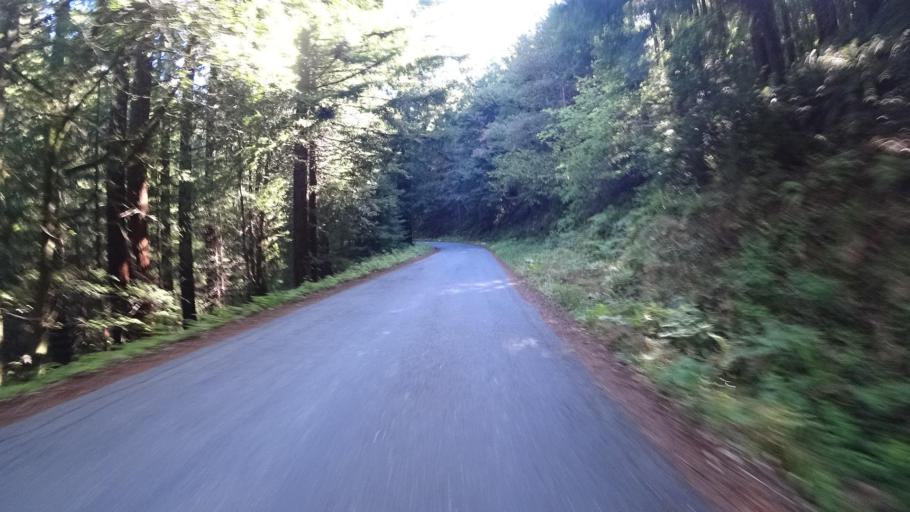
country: US
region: California
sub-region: Humboldt County
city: Rio Dell
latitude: 40.4570
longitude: -123.9946
